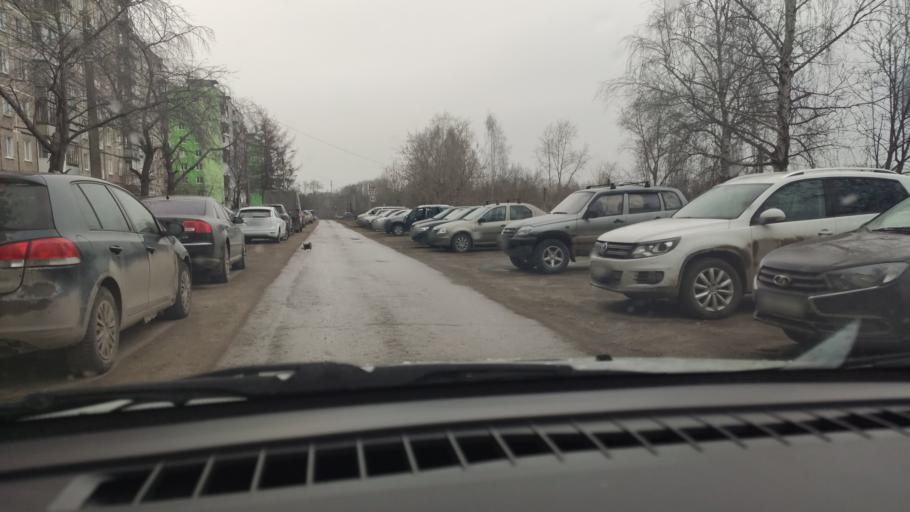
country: RU
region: Perm
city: Perm
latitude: 58.1113
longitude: 56.3809
